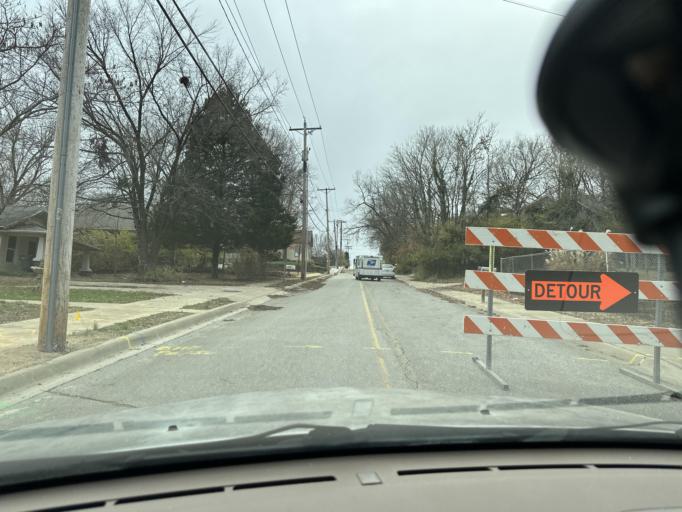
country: US
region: Arkansas
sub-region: Washington County
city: Fayetteville
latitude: 36.0608
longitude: -94.1565
